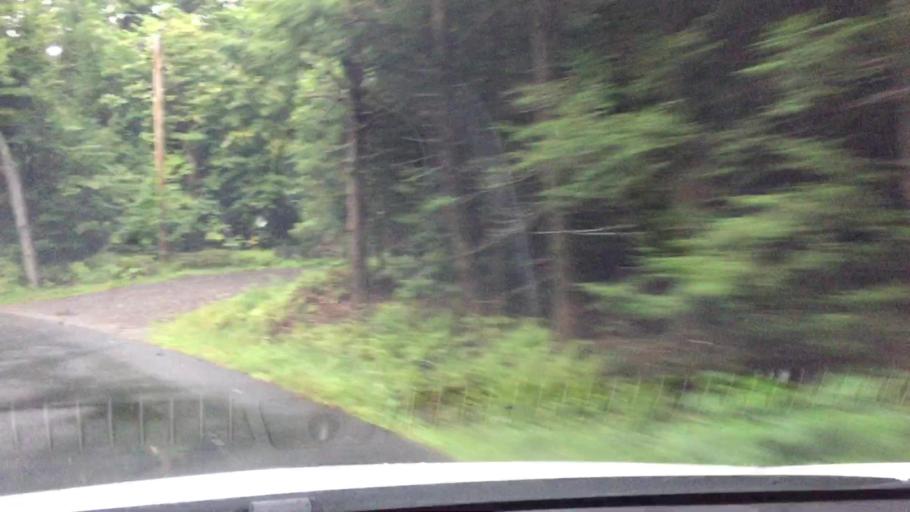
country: US
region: Massachusetts
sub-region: Berkshire County
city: Otis
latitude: 42.1502
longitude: -73.0542
